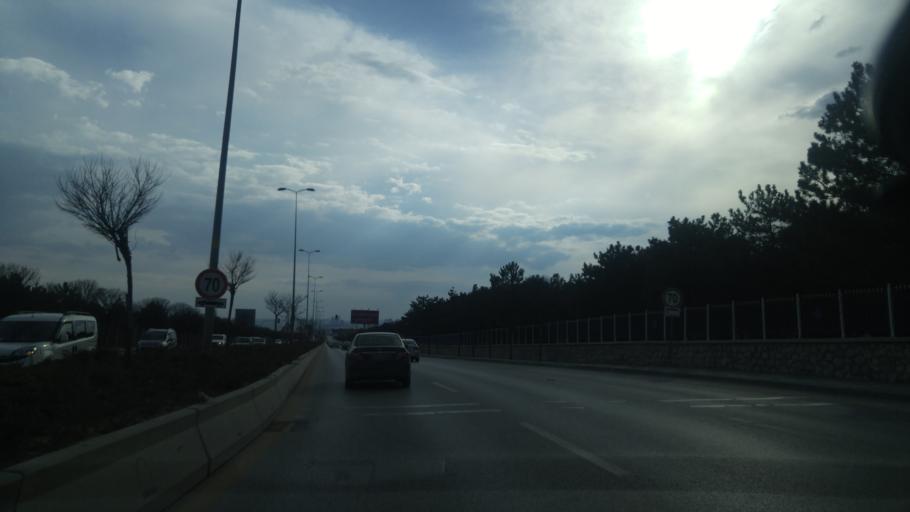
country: TR
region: Ankara
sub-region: Goelbasi
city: Golbasi
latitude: 39.8437
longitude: 32.7808
